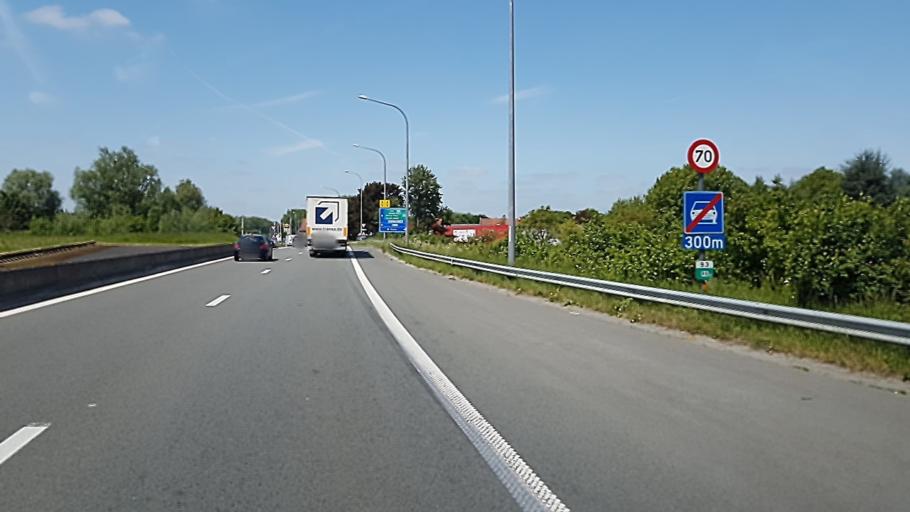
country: BE
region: Flanders
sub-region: Provincie West-Vlaanderen
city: Kuurne
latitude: 50.8426
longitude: 3.2763
